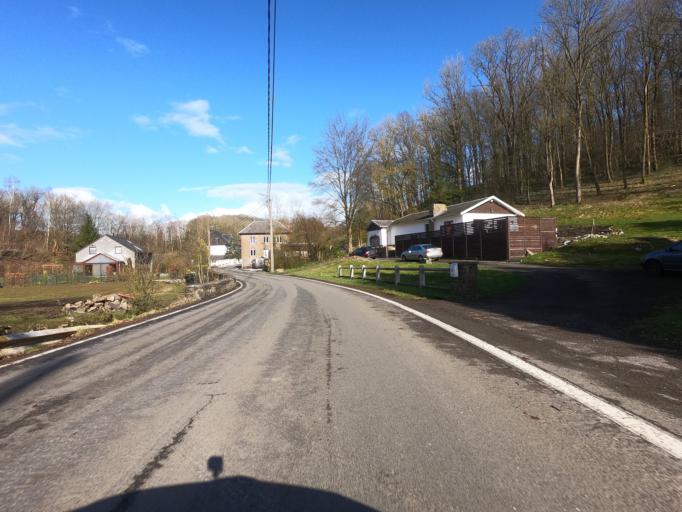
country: BE
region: Wallonia
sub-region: Province de Namur
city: Mettet
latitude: 50.3008
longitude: 4.7356
